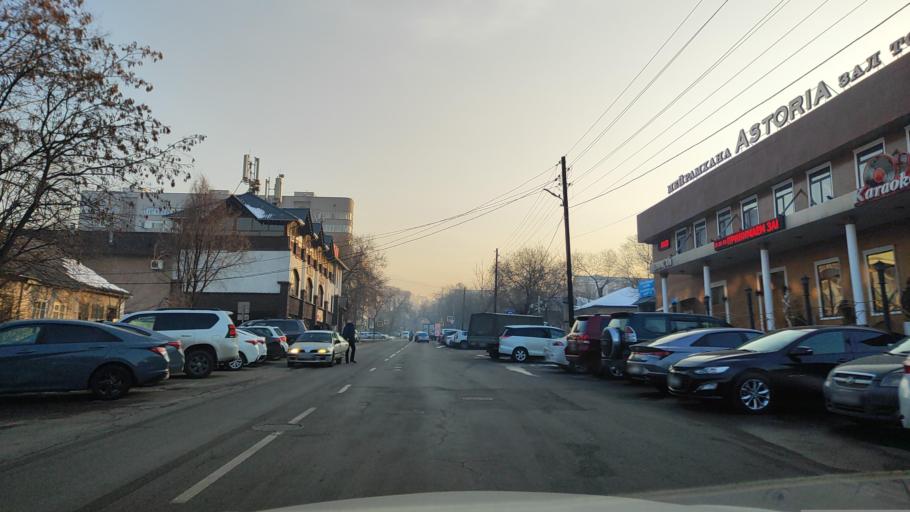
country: KZ
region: Almaty Qalasy
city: Almaty
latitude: 43.2570
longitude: 76.9602
